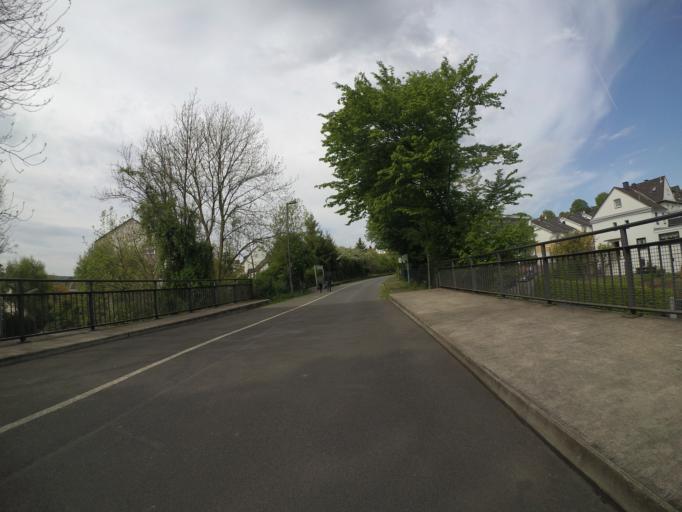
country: DE
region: North Rhine-Westphalia
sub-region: Regierungsbezirk Dusseldorf
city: Wuppertal
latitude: 51.2672
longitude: 7.1590
